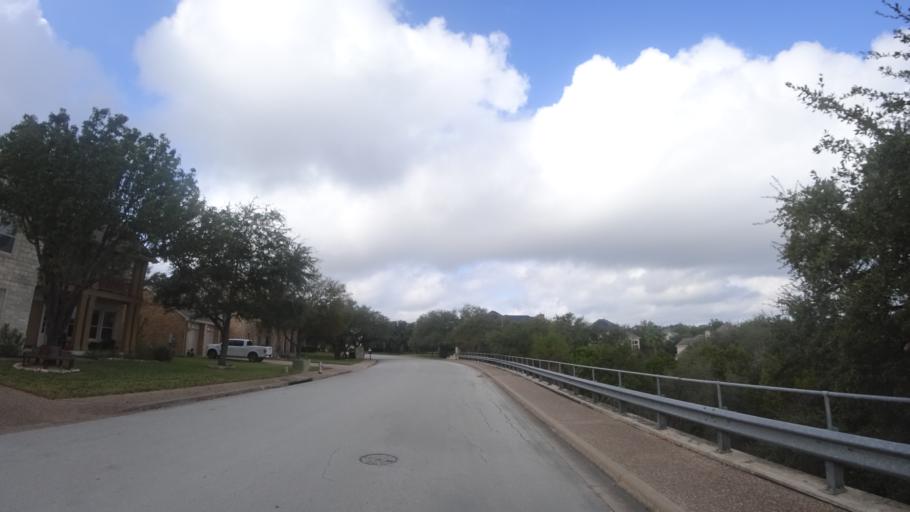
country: US
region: Texas
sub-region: Travis County
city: Barton Creek
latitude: 30.3112
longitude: -97.8959
